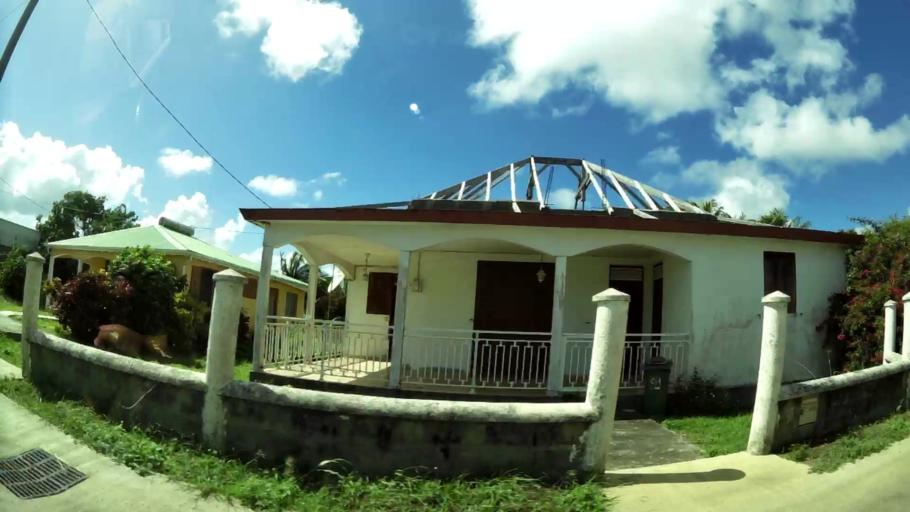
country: GP
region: Guadeloupe
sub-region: Guadeloupe
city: Petit-Canal
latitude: 16.4132
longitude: -61.4702
